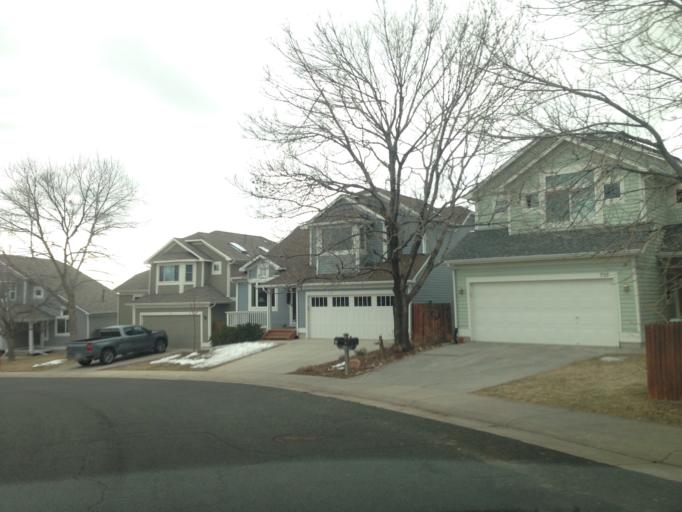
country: US
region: Colorado
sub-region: Boulder County
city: Louisville
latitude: 39.9767
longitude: -105.1517
